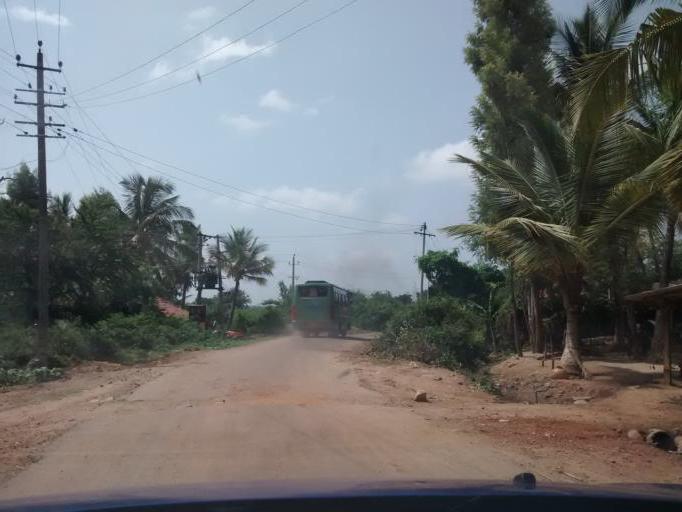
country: IN
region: Karnataka
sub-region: Hassan
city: Hole Narsipur
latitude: 12.6997
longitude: 76.1647
